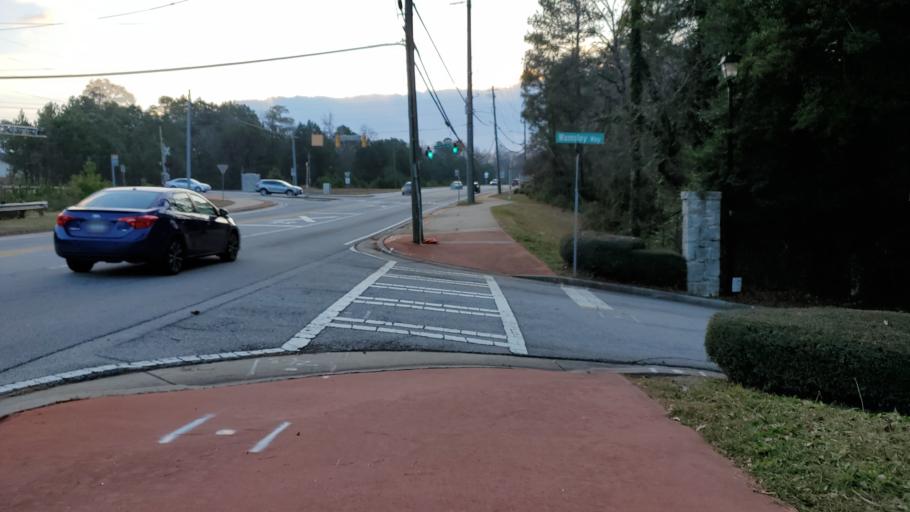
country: US
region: Georgia
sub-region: DeKalb County
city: Clarkston
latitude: 33.8193
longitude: -84.2109
